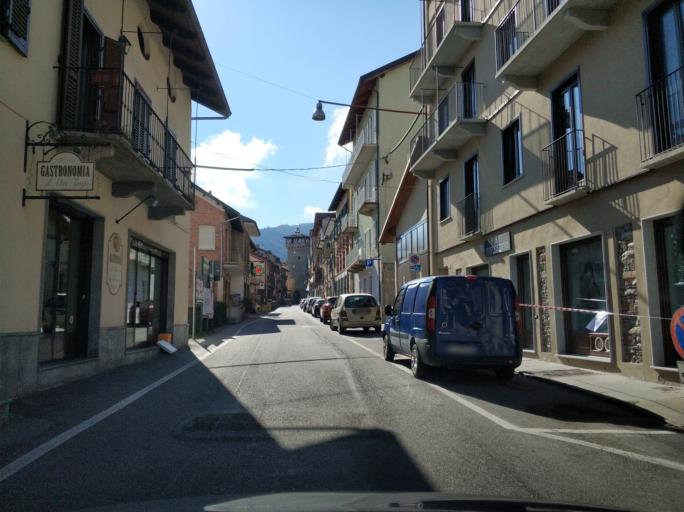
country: IT
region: Piedmont
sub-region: Provincia di Torino
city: Lanzo Torinese
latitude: 45.2745
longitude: 7.4738
